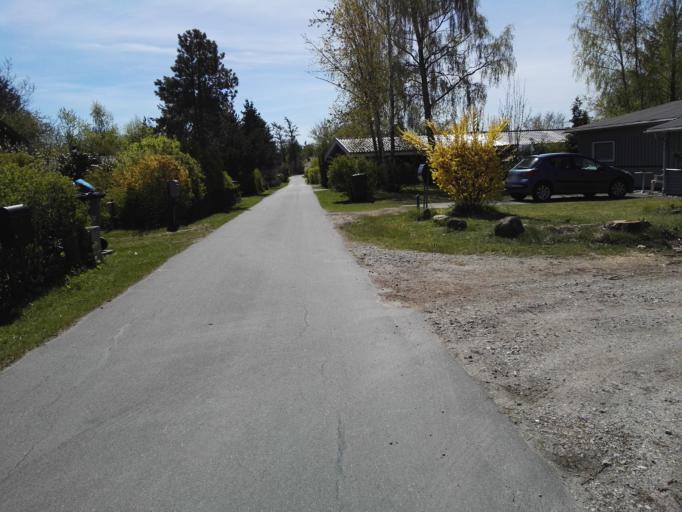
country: DK
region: Capital Region
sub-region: Frederikssund Kommune
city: Frederikssund
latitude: 55.8960
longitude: 12.0519
